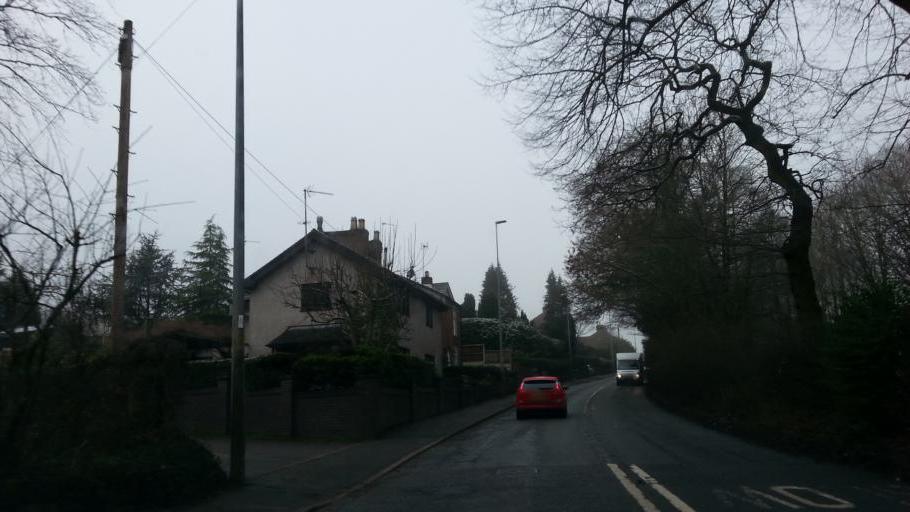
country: GB
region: England
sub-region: Staffordshire
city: Biddulph
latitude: 53.1488
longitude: -2.1774
